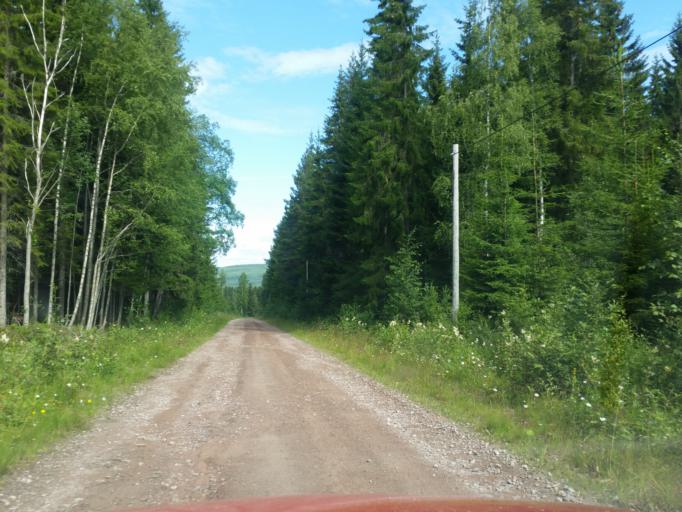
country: SE
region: Dalarna
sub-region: Gagnefs Kommun
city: Gagnef
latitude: 60.6494
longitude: 15.1650
